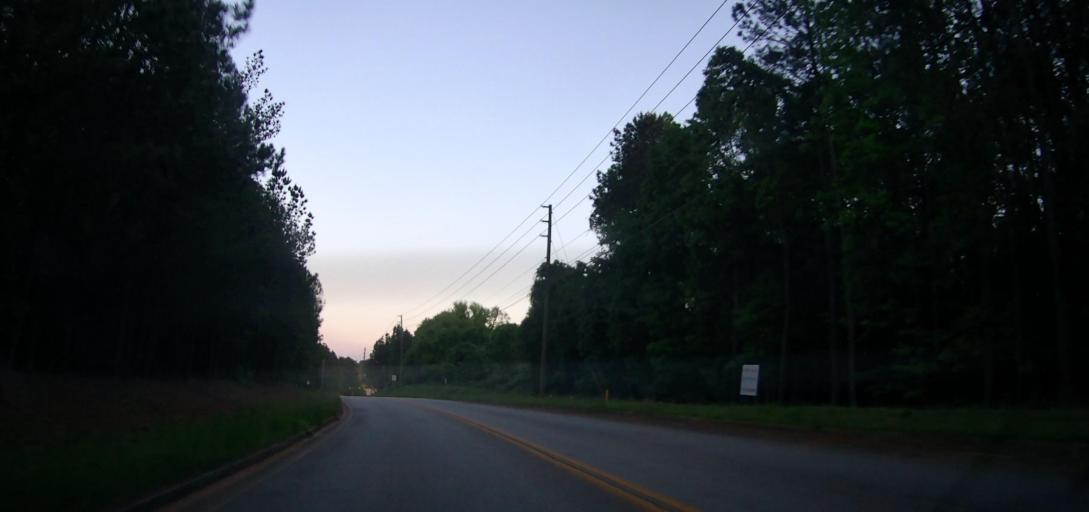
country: US
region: Georgia
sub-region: Henry County
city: Stockbridge
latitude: 33.4853
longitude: -84.2144
